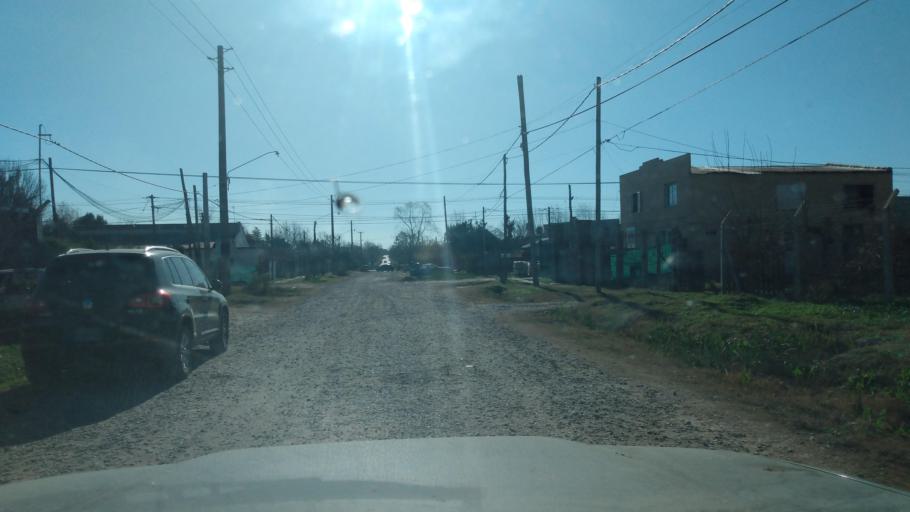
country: AR
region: Buenos Aires
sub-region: Partido de Lujan
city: Lujan
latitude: -34.5733
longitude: -59.0787
